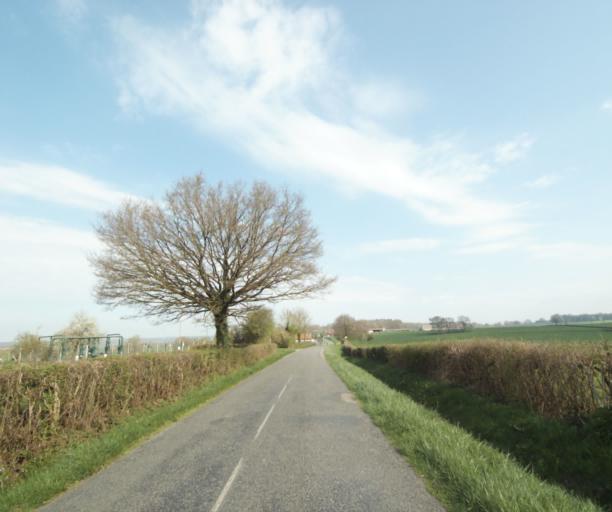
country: FR
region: Bourgogne
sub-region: Departement de Saone-et-Loire
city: Palinges
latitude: 46.5063
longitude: 4.2069
